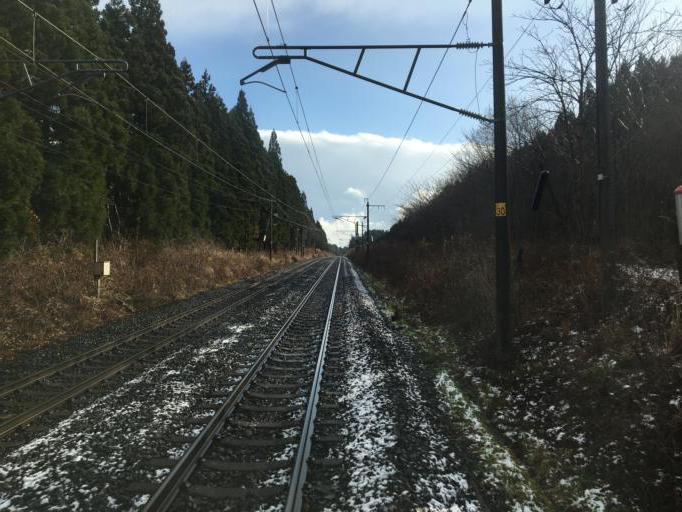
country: JP
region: Aomori
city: Aomori Shi
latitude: 40.9101
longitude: 141.0514
